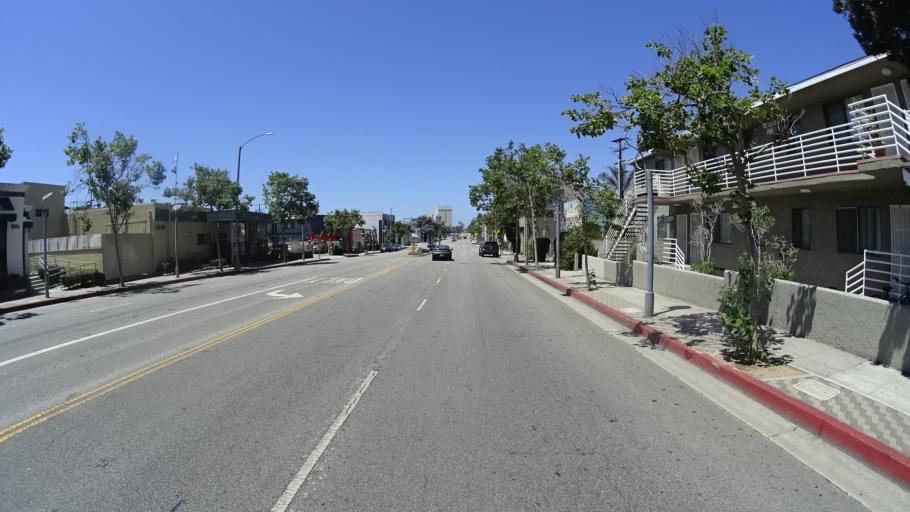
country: US
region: California
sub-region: Los Angeles County
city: Santa Monica
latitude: 34.0141
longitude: -118.4798
